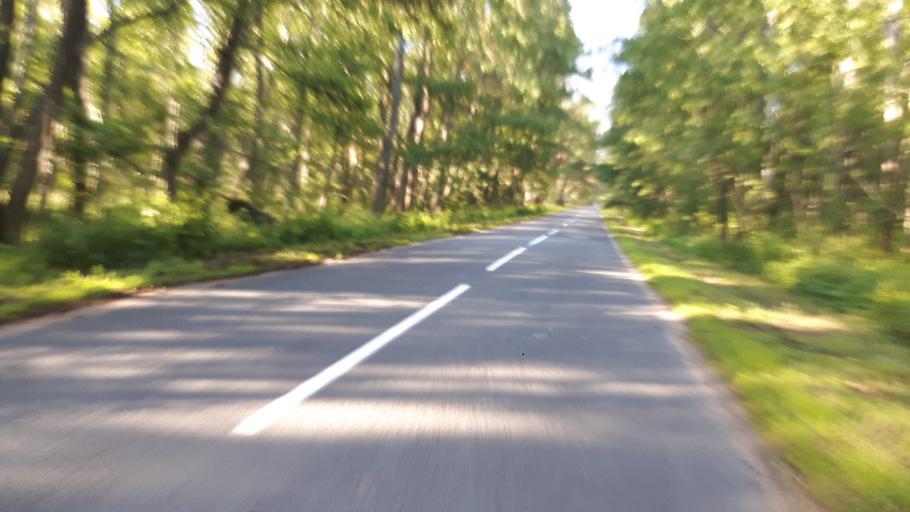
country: LT
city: Nida
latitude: 55.2488
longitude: 20.9245
